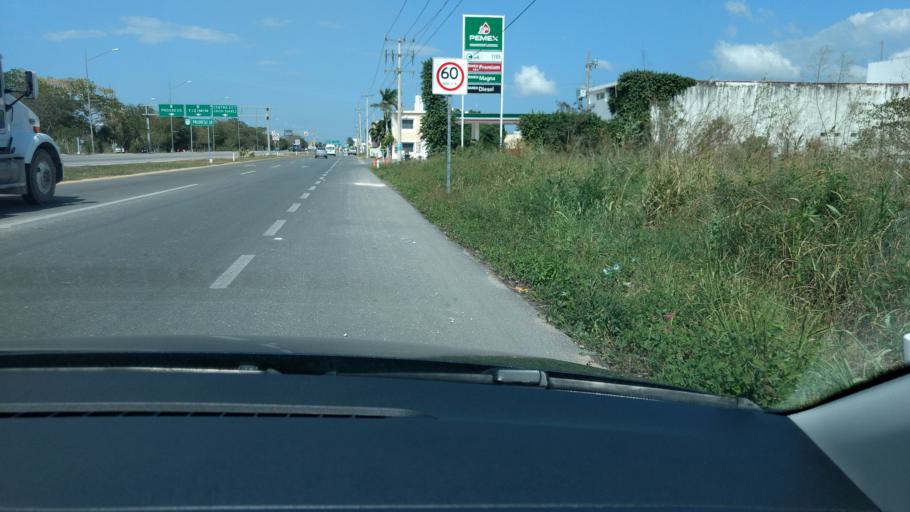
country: MX
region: Yucatan
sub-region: Kanasin
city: Kanasin
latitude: 20.9885
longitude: -89.5625
